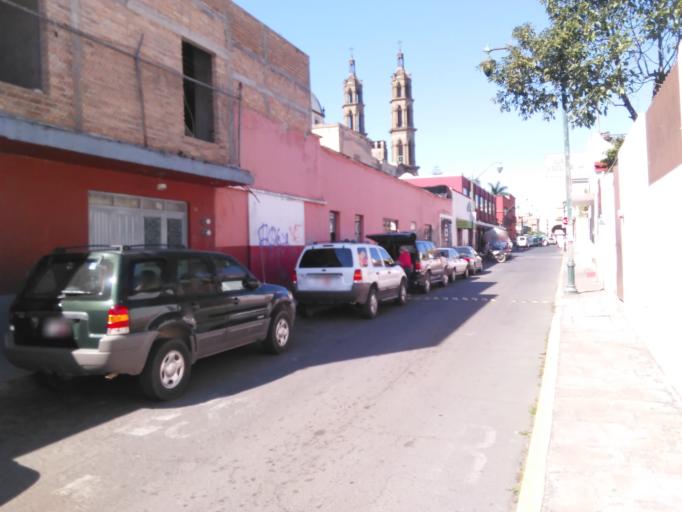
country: MX
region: Nayarit
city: Tepic
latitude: 21.5118
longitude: -104.8900
